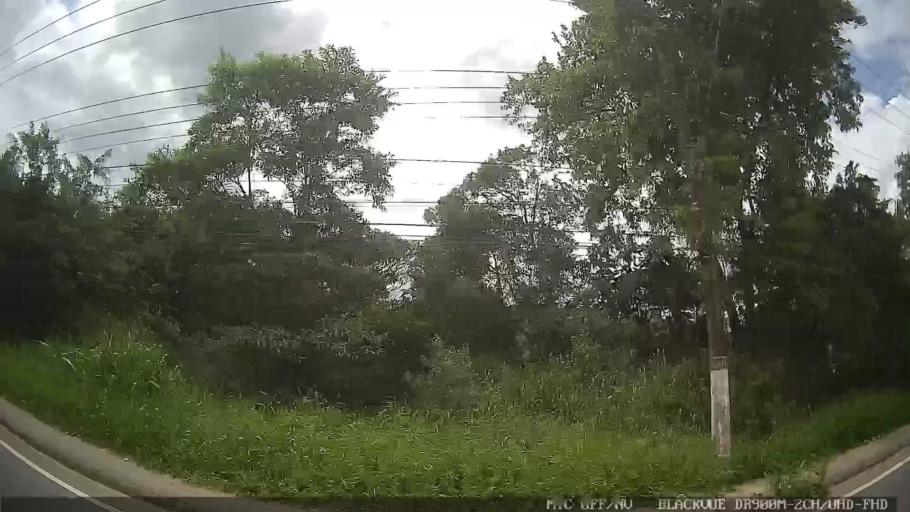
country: BR
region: Sao Paulo
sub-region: Ribeirao Pires
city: Ribeirao Pires
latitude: -23.6811
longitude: -46.3583
